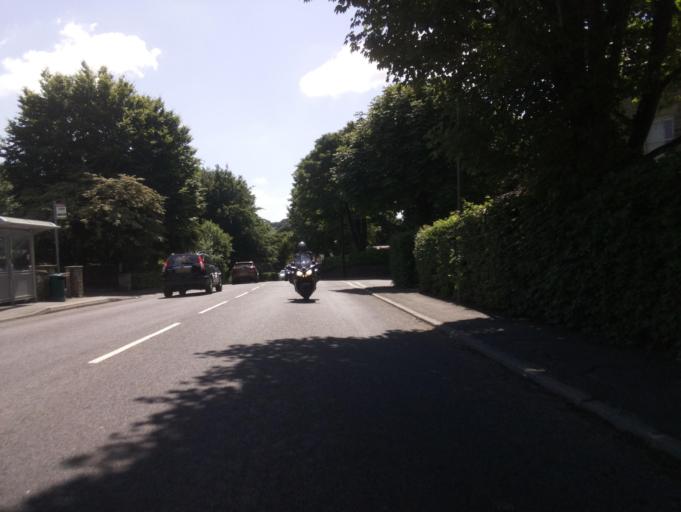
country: GB
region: England
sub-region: Derbyshire
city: Buxton
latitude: 53.2490
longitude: -1.9104
